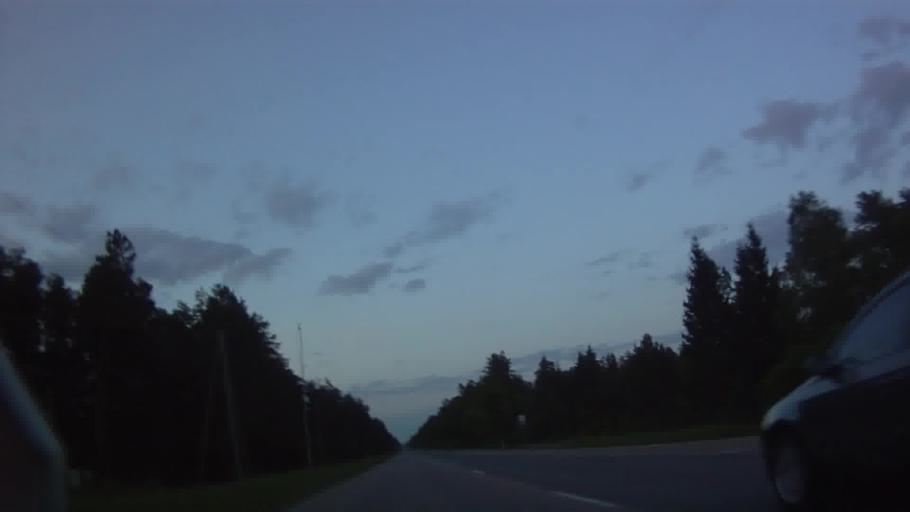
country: LV
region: Incukalns
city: Vangazi
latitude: 57.0688
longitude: 24.4893
